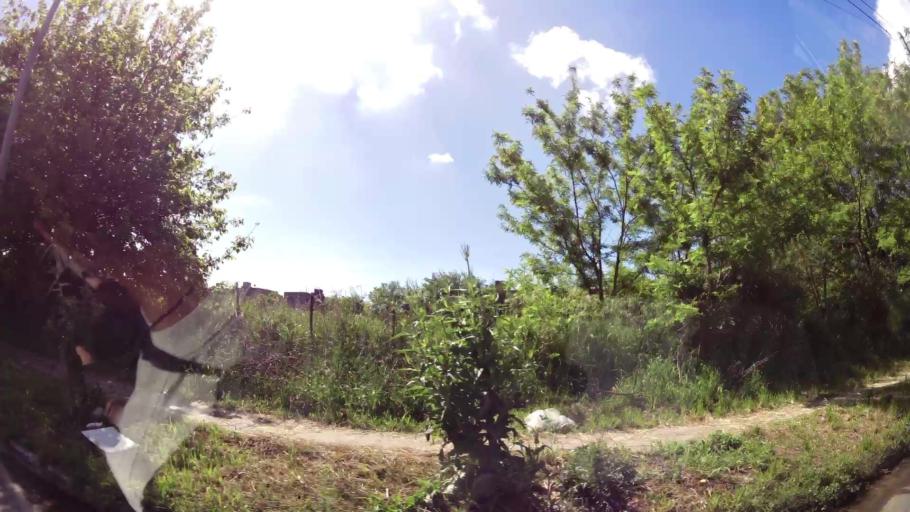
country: AR
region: Buenos Aires
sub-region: Partido de Quilmes
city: Quilmes
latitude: -34.8143
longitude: -58.2686
